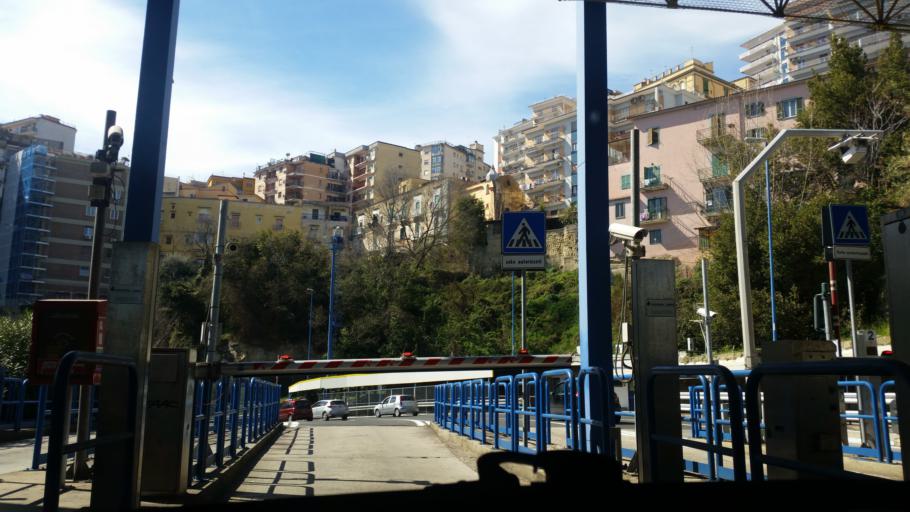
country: IT
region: Campania
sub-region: Provincia di Napoli
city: Napoli
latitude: 40.8585
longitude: 14.2332
